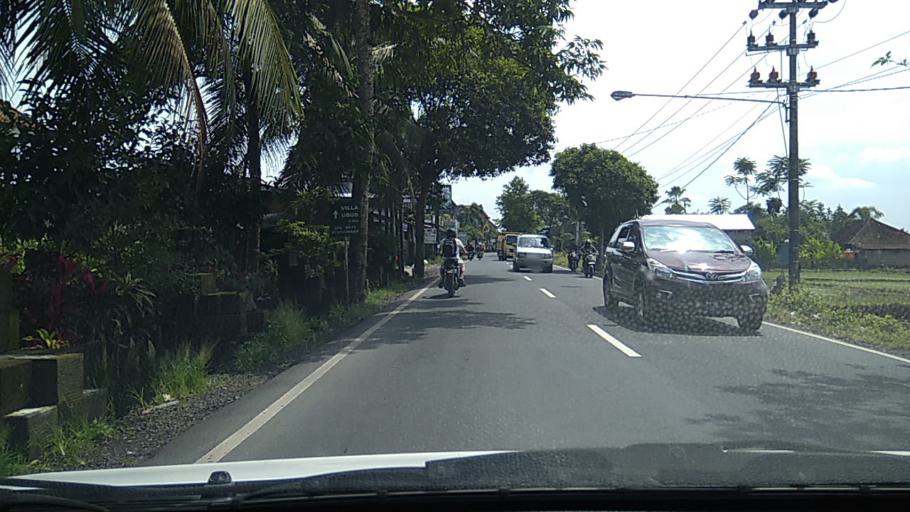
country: ID
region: Bali
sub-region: Kabupaten Gianyar
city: Ubud
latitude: -8.5232
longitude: 115.2767
